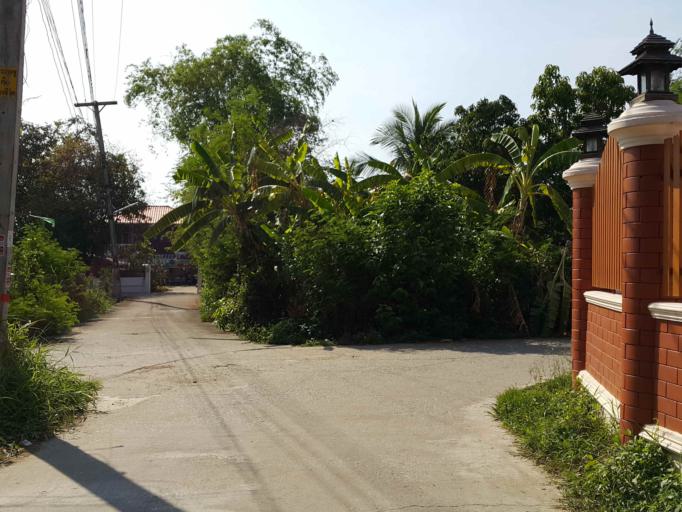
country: TH
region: Chiang Mai
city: San Kamphaeng
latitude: 18.7748
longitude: 99.1163
